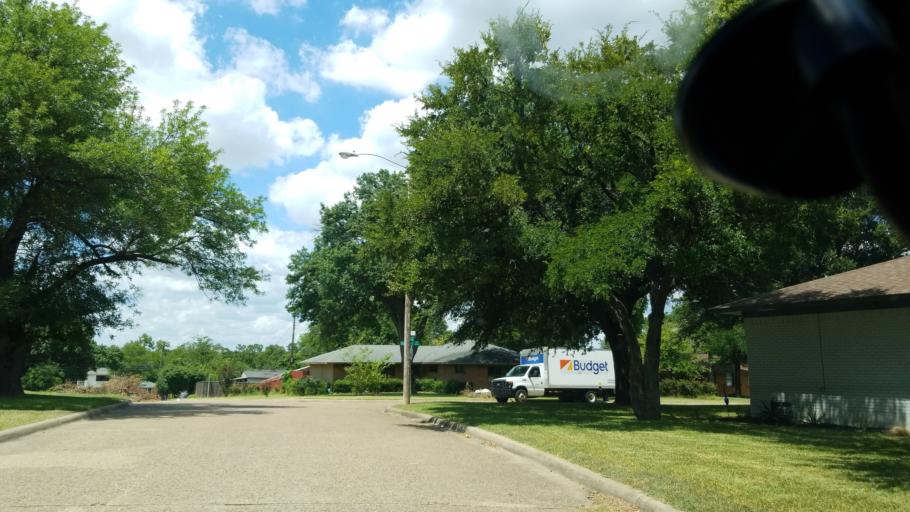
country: US
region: Texas
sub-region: Dallas County
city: Cockrell Hill
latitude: 32.7035
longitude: -96.8622
